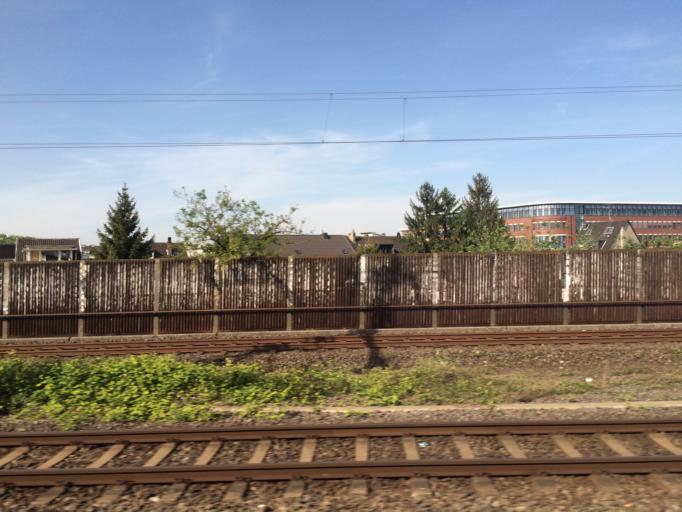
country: DE
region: North Rhine-Westphalia
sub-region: Regierungsbezirk Koln
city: Humboldtkolonie
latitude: 50.9346
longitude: 6.9993
